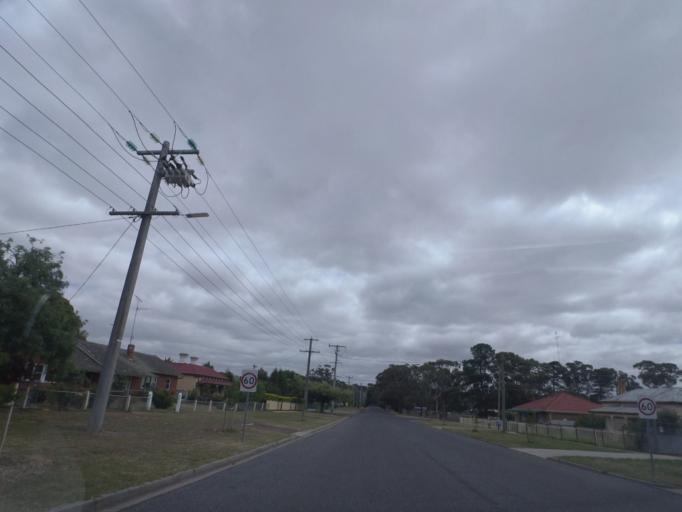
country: AU
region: Victoria
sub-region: Whittlesea
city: Whittlesea
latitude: -37.2051
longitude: 145.0450
